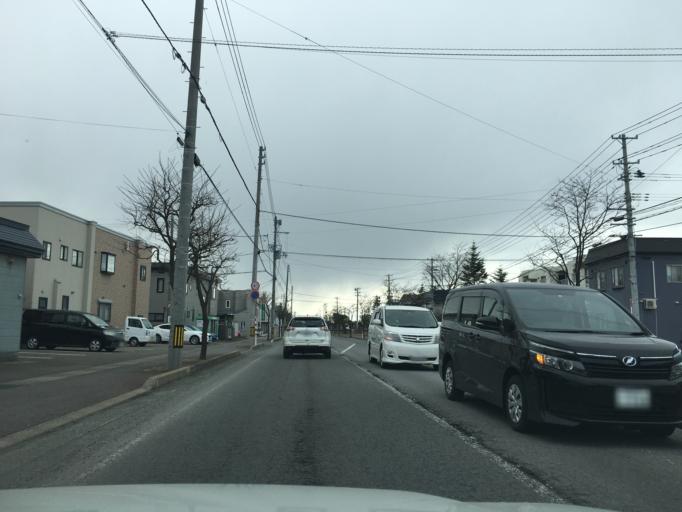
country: JP
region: Aomori
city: Aomori Shi
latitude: 40.8351
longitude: 140.7958
